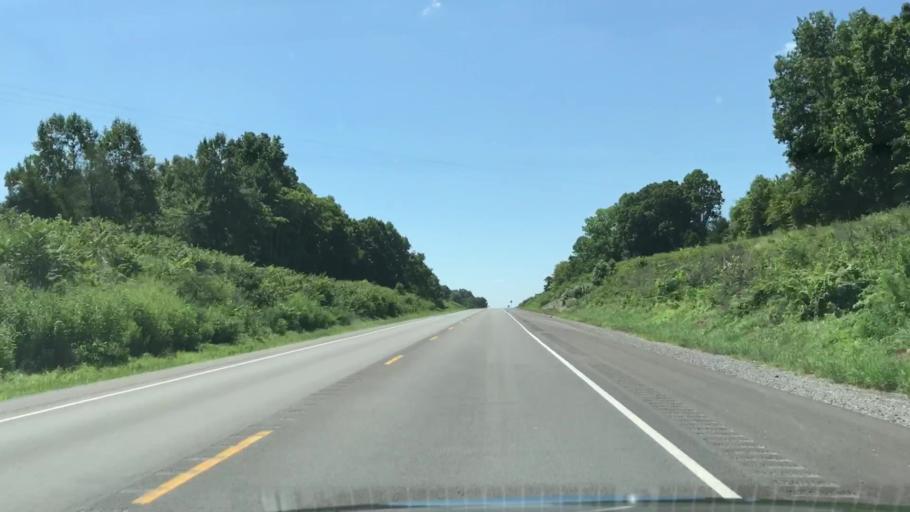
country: US
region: Kentucky
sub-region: Cumberland County
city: Burkesville
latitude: 36.6614
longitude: -85.3706
